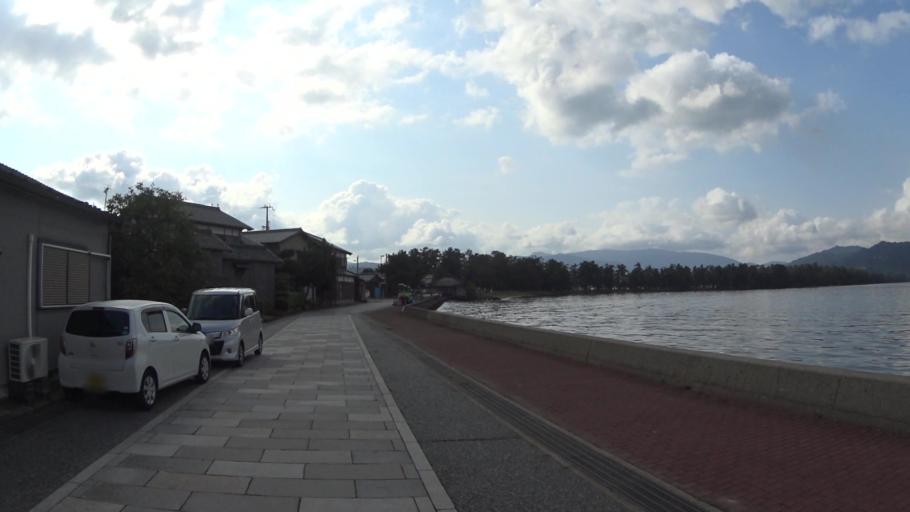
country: JP
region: Kyoto
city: Miyazu
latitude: 35.5802
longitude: 135.1970
